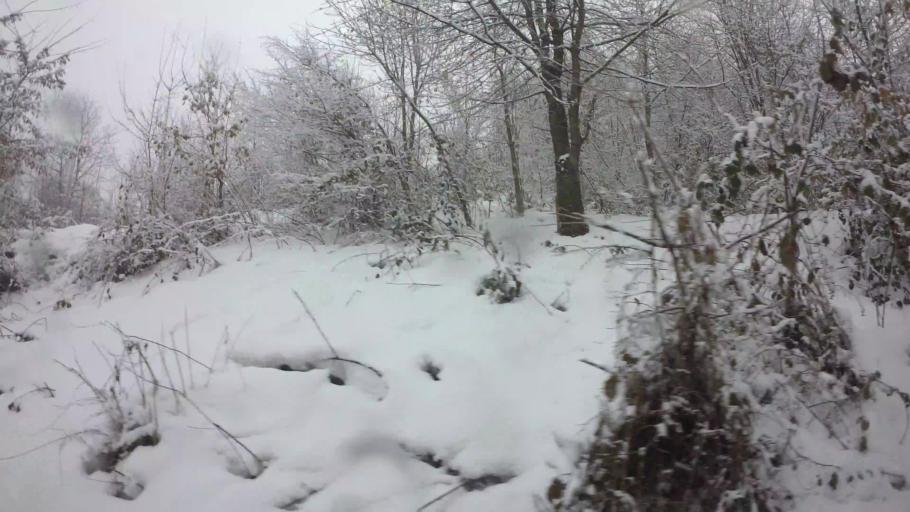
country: BA
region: Federation of Bosnia and Herzegovina
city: Kobilja Glava
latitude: 43.8525
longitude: 18.4431
